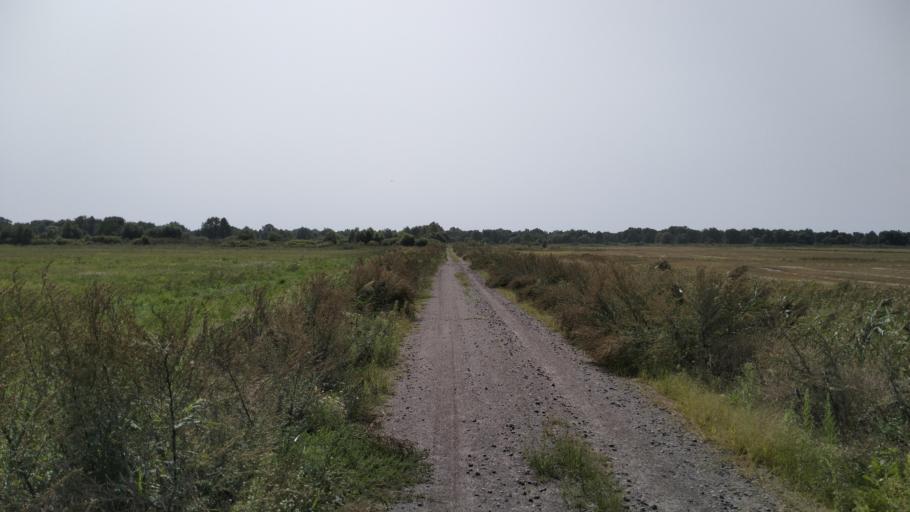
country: BY
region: Brest
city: Davyd-Haradok
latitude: 51.9710
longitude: 27.1739
